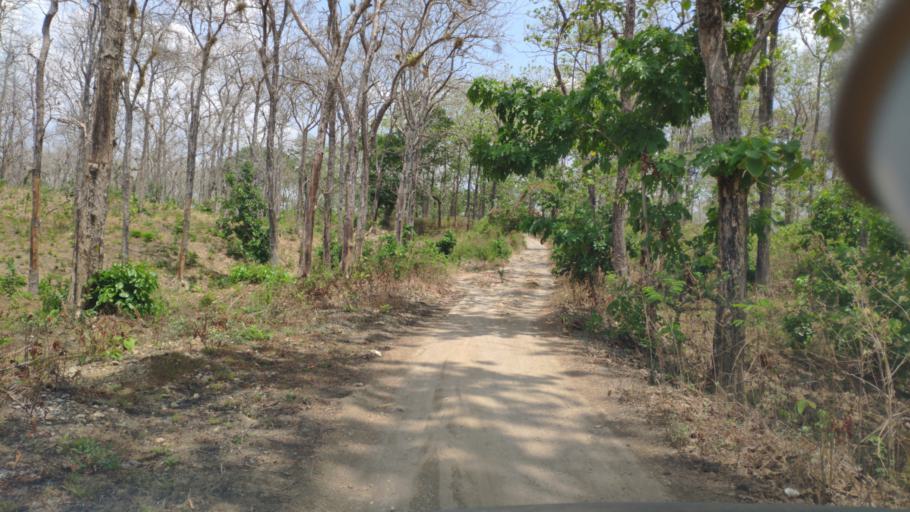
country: ID
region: Central Java
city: Suruhan
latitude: -6.9940
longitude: 111.5285
